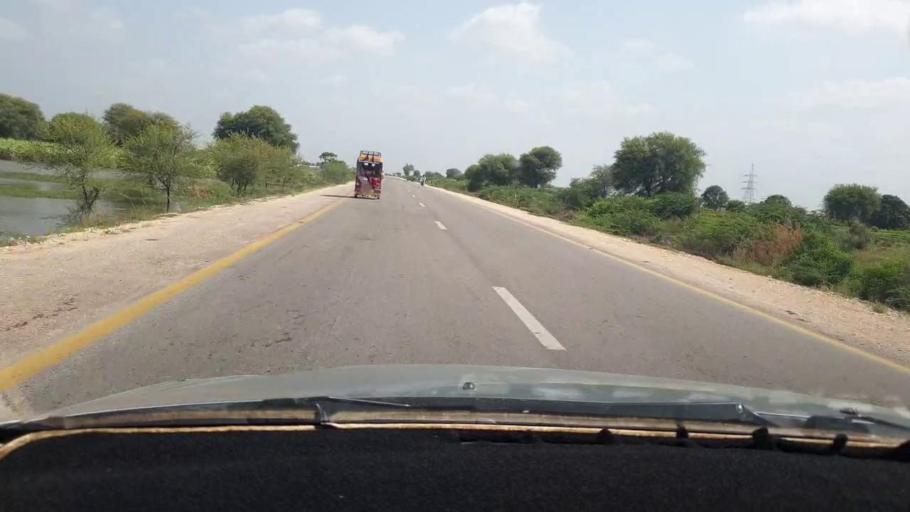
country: PK
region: Sindh
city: Digri
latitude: 25.1046
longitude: 69.1681
